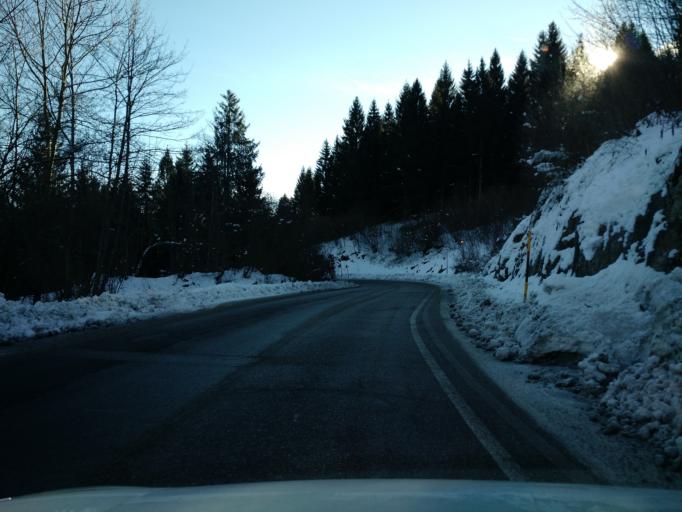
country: IT
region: Veneto
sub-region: Provincia di Vicenza
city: Canove di Roana
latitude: 45.8380
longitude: 11.4452
